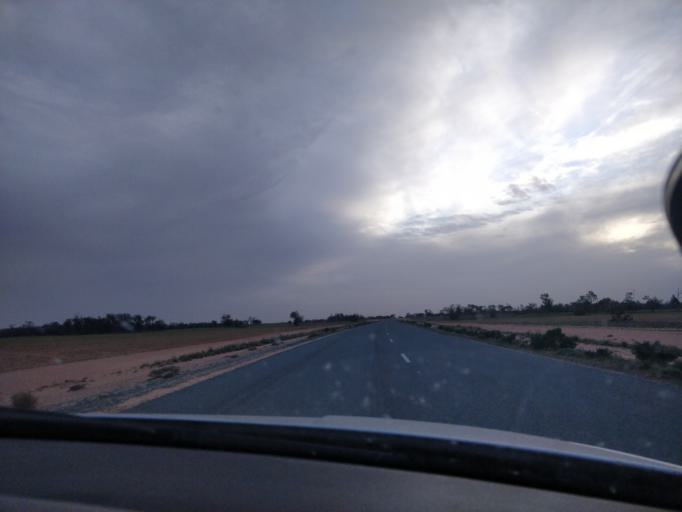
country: AU
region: New South Wales
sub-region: Wentworth
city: Gol Gol
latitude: -34.0364
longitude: 142.3663
